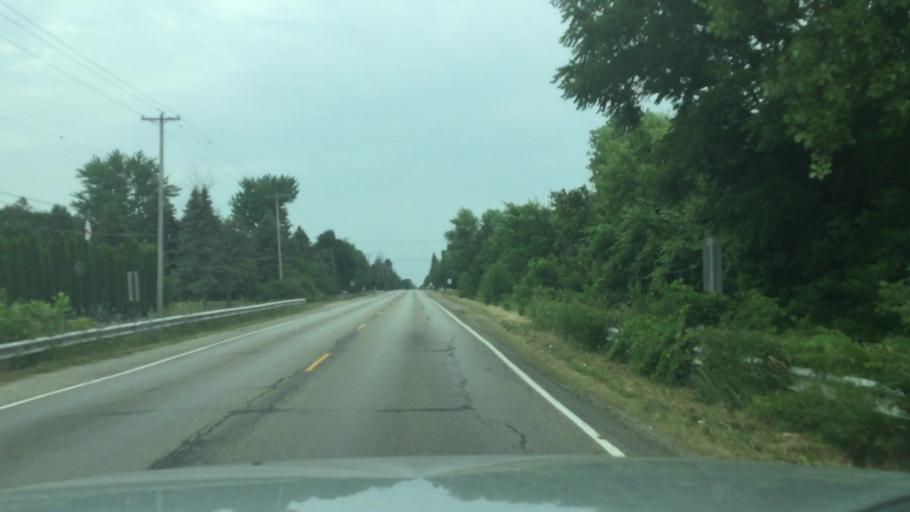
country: US
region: Michigan
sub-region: Genesee County
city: Flint
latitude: 42.9595
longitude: -83.6981
